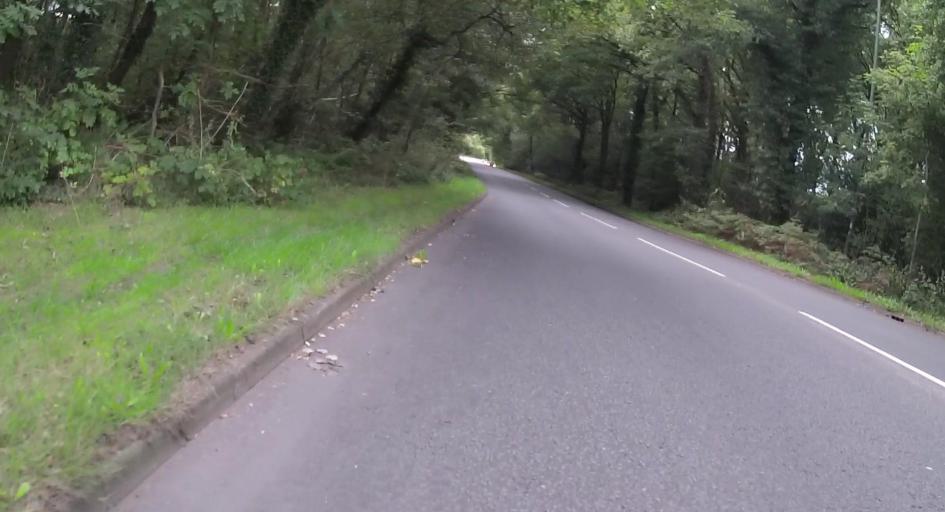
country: GB
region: England
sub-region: Surrey
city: Chobham
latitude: 51.3281
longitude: -0.5863
